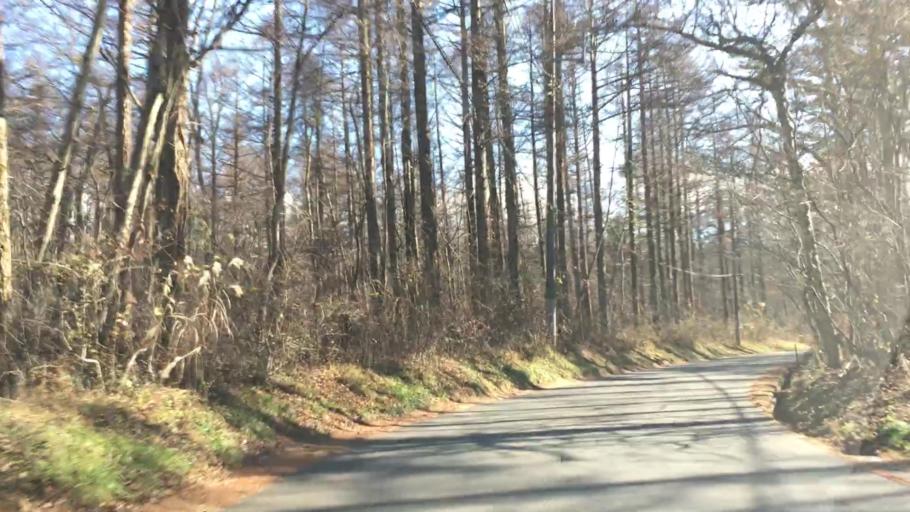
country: JP
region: Shizuoka
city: Gotemba
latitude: 35.4055
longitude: 138.8643
